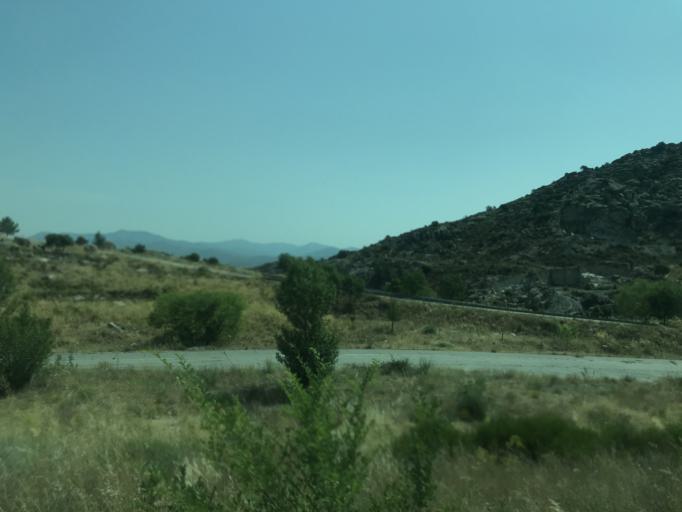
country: ES
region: Madrid
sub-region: Provincia de Madrid
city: La Cabrera
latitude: 40.8897
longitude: -3.6004
